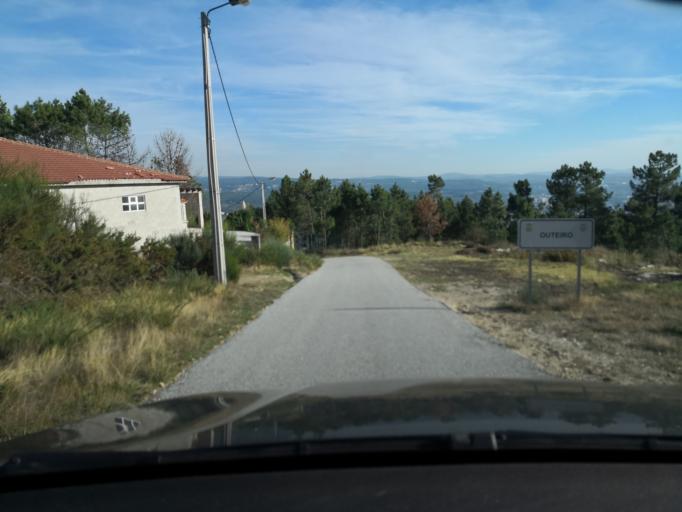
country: PT
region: Vila Real
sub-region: Vila Real
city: Vila Real
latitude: 41.3405
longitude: -7.7503
